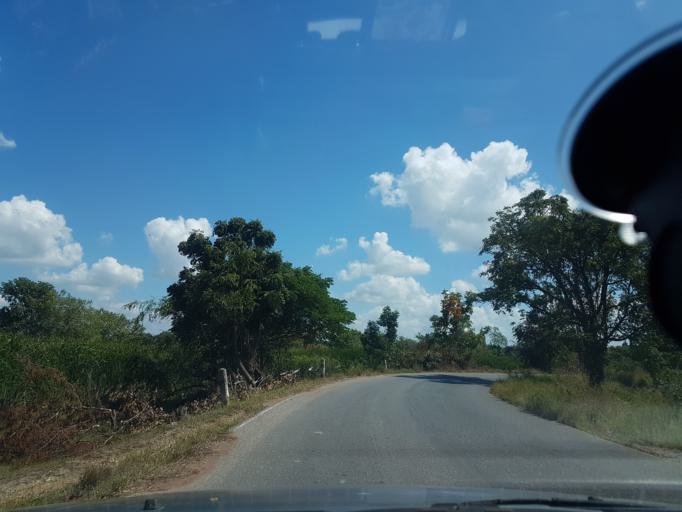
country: TH
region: Lop Buri
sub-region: Amphoe Tha Luang
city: Tha Luang
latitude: 14.9994
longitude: 101.0071
